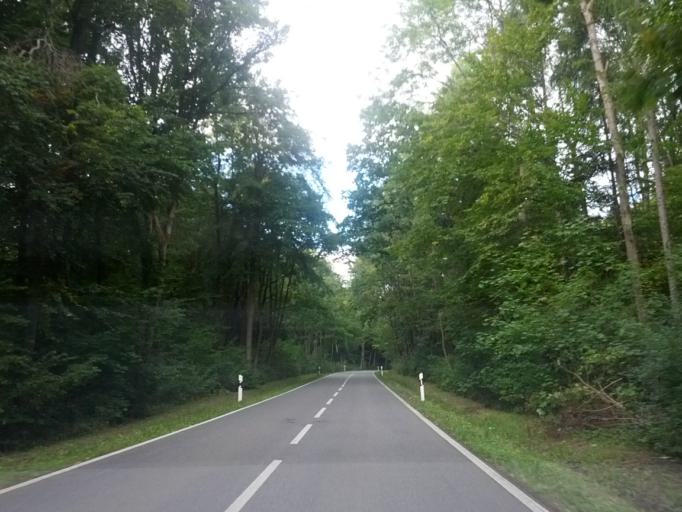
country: DE
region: Hesse
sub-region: Regierungsbezirk Kassel
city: Weissenborn
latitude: 51.0607
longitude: 10.1071
